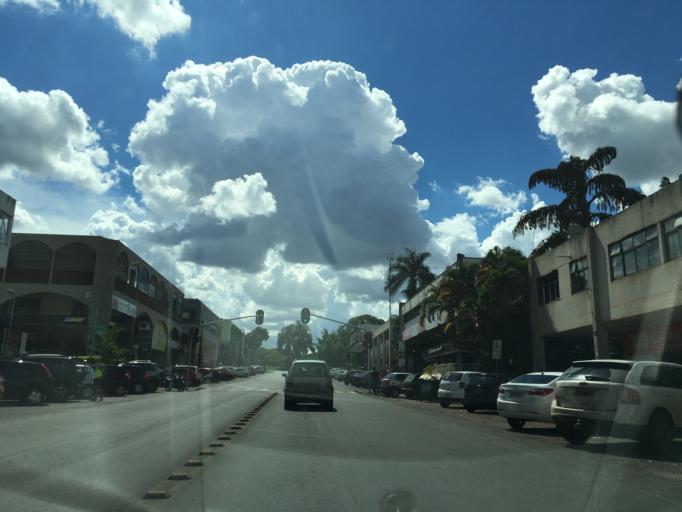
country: BR
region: Federal District
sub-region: Brasilia
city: Brasilia
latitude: -15.7800
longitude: -47.8753
